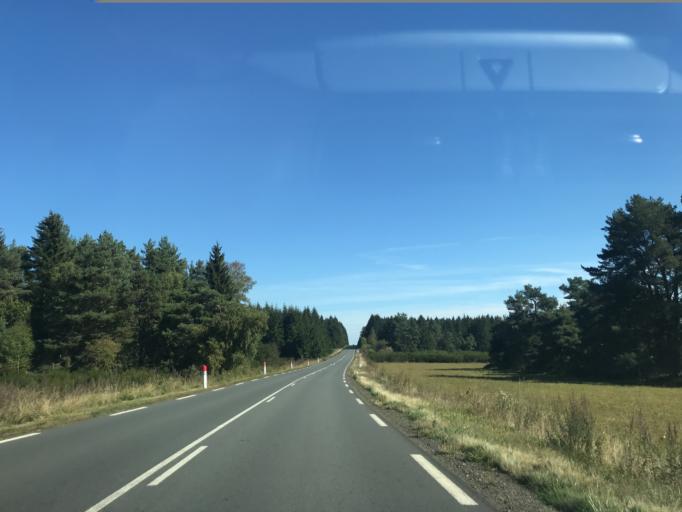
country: FR
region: Auvergne
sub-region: Departement du Puy-de-Dome
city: Orcines
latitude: 45.7506
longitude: 2.9635
